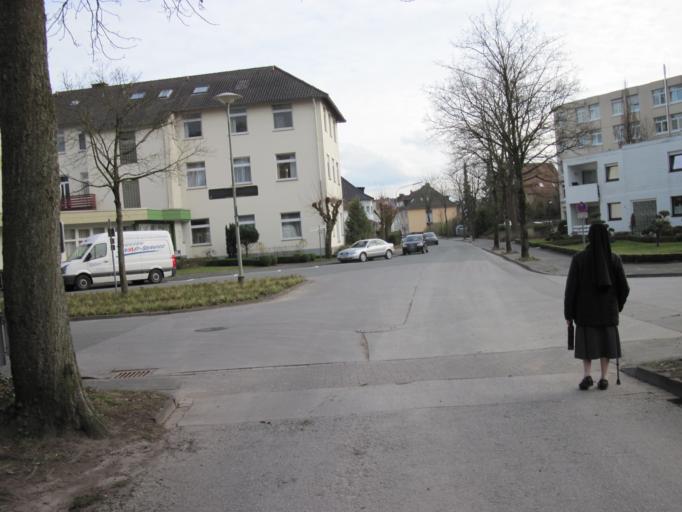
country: DE
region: North Rhine-Westphalia
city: Bad Lippspringe
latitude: 51.7883
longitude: 8.8183
